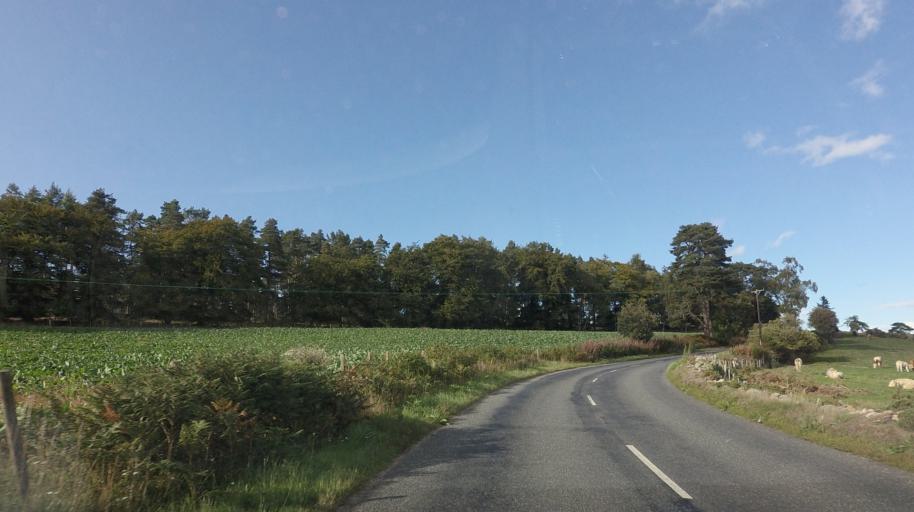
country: GB
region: Scotland
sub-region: Aberdeenshire
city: Banchory
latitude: 57.1198
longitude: -2.4278
